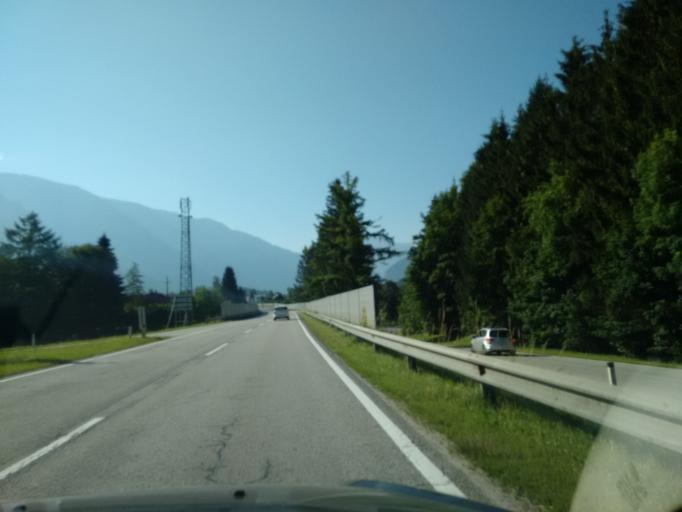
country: AT
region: Upper Austria
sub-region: Politischer Bezirk Gmunden
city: Bad Goisern
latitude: 47.6330
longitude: 13.6291
